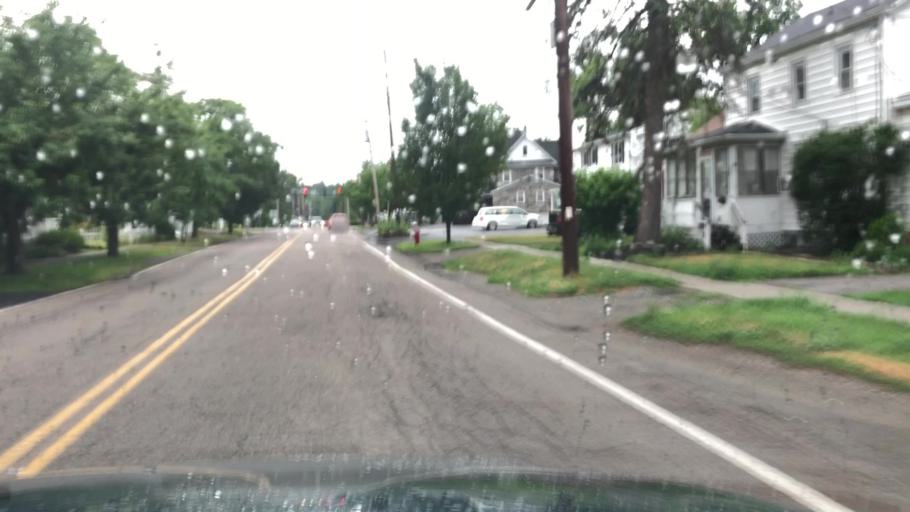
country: US
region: New York
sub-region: Dutchess County
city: Fishkill
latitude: 41.5330
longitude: -73.9038
